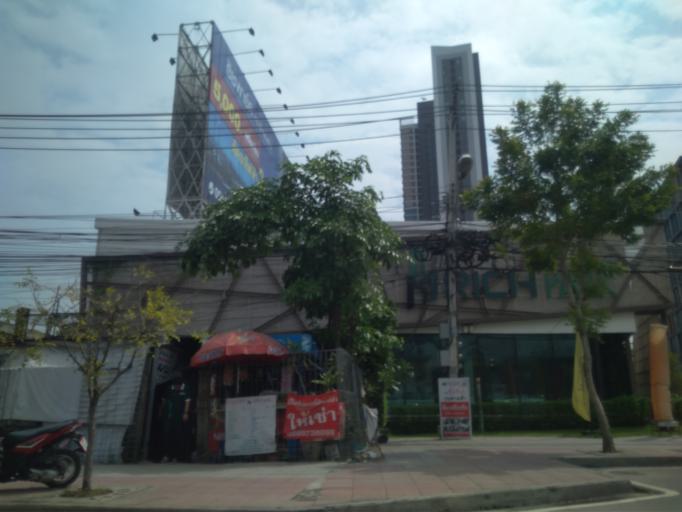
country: TH
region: Bangkok
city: Suan Luang
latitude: 13.7378
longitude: 100.6417
